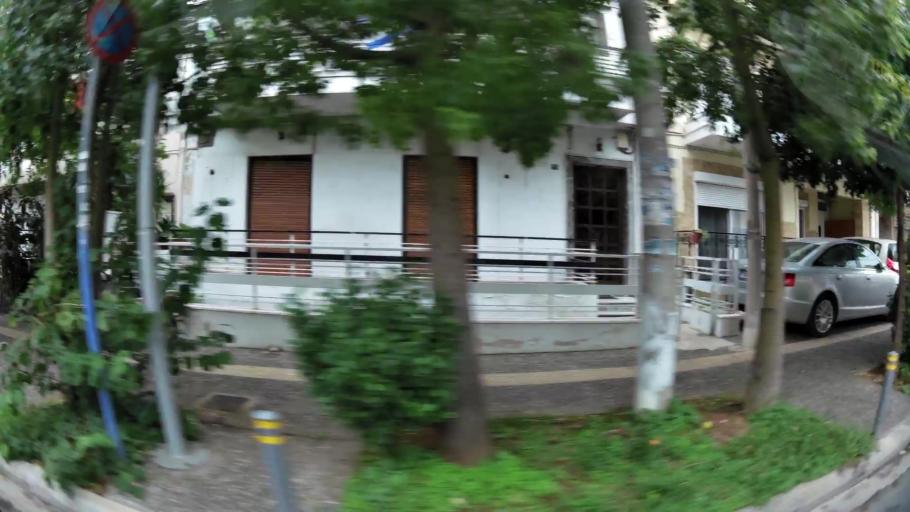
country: GR
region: Attica
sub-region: Nomos Piraios
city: Korydallos
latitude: 37.9819
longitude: 23.6391
